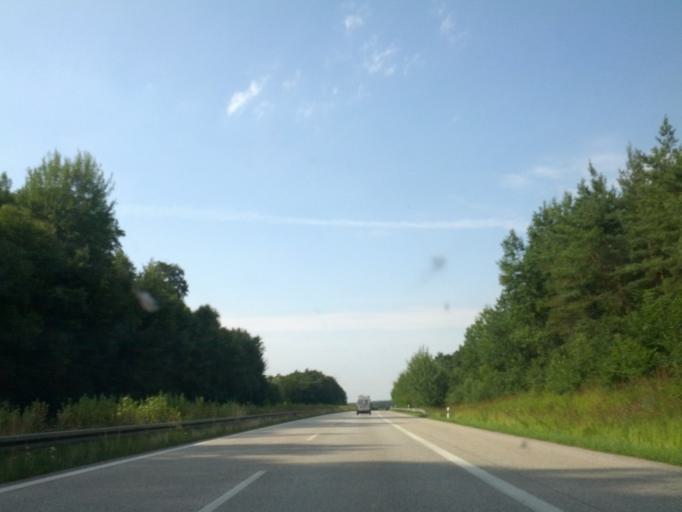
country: DE
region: Mecklenburg-Vorpommern
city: Lalendorf
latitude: 53.7487
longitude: 12.3309
